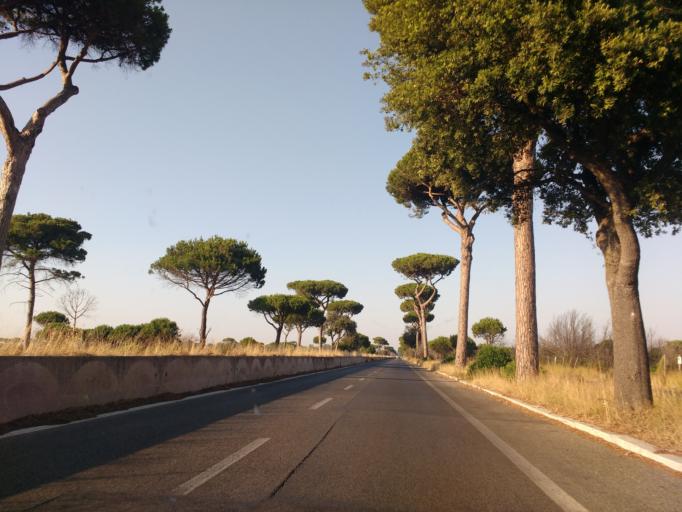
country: IT
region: Latium
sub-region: Citta metropolitana di Roma Capitale
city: Acilia-Castel Fusano-Ostia Antica
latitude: 41.7252
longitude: 12.3311
